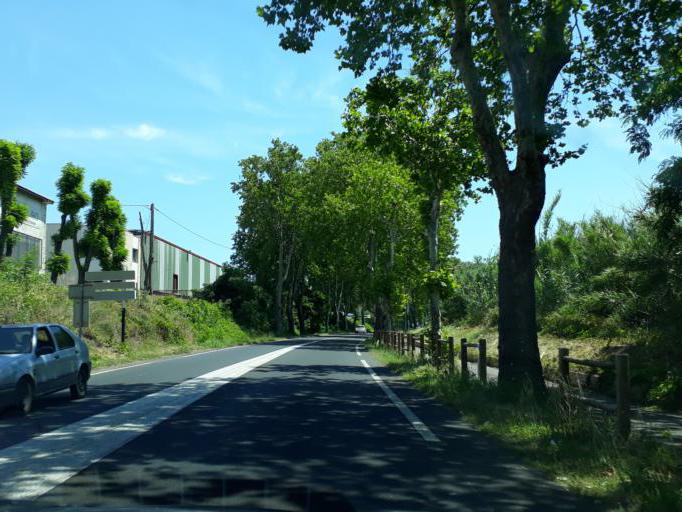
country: FR
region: Languedoc-Roussillon
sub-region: Departement de l'Herault
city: Beziers
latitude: 43.3310
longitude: 3.2388
